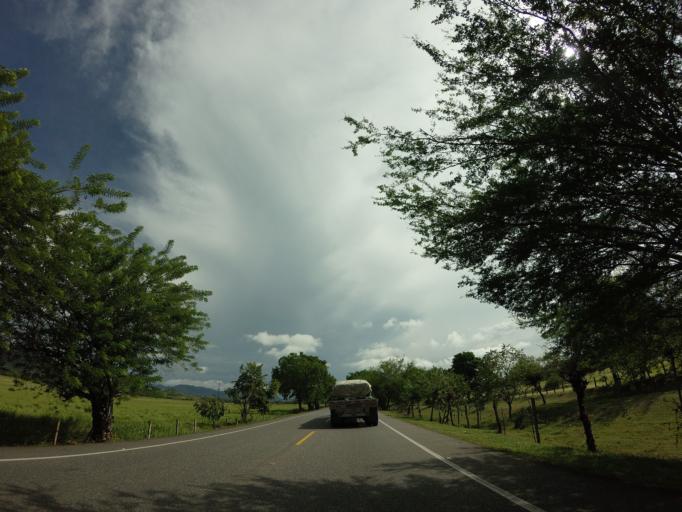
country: CO
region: Tolima
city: Honda
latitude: 5.3275
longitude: -74.7396
